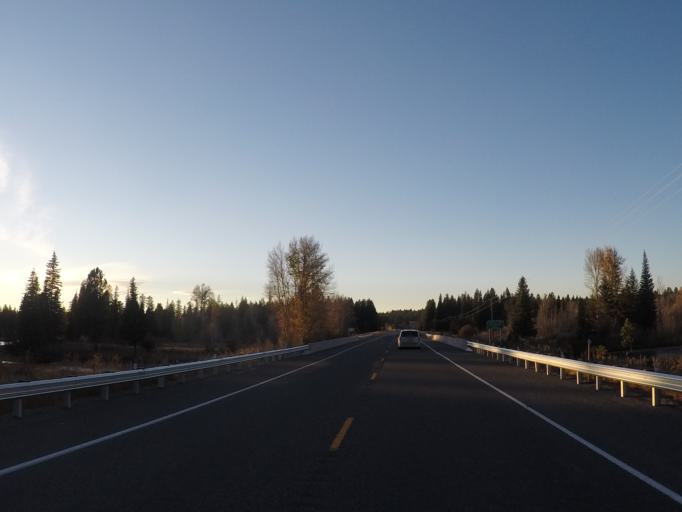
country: US
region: Montana
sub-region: Lewis and Clark County
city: Lincoln
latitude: 46.9999
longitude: -113.0356
